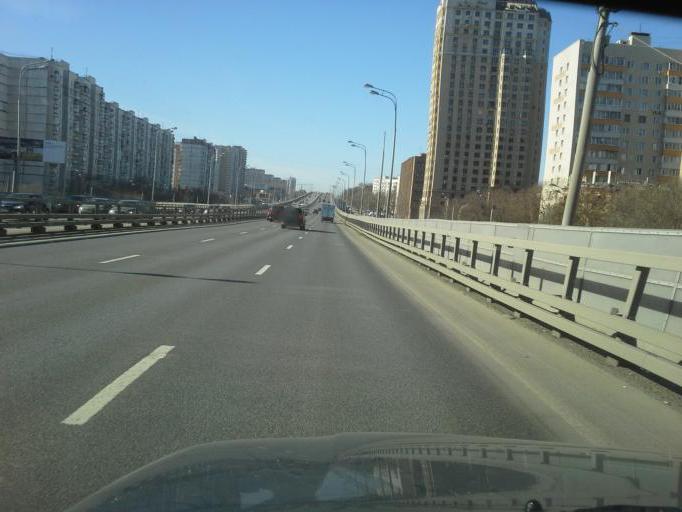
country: RU
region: Moskovskaya
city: Bol'shaya Setun'
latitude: 55.7192
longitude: 37.4190
